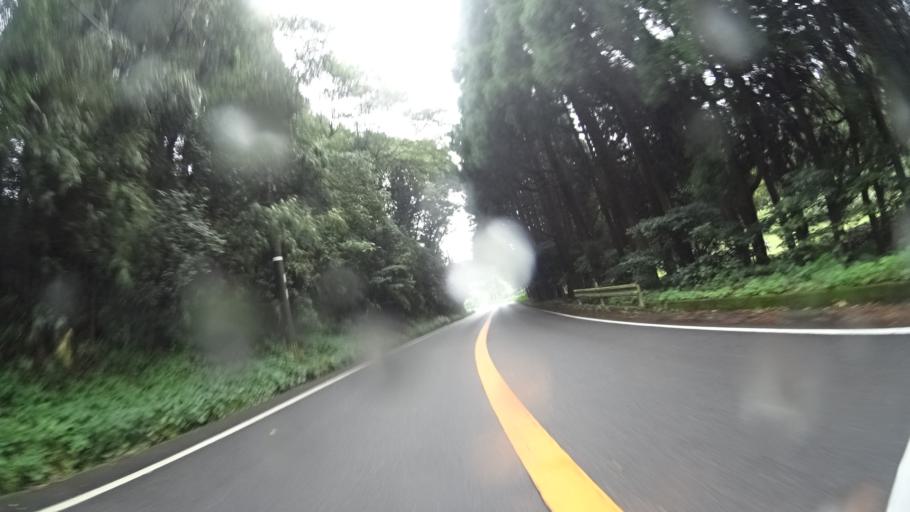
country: JP
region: Kagoshima
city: Kajiki
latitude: 31.7799
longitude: 130.6723
